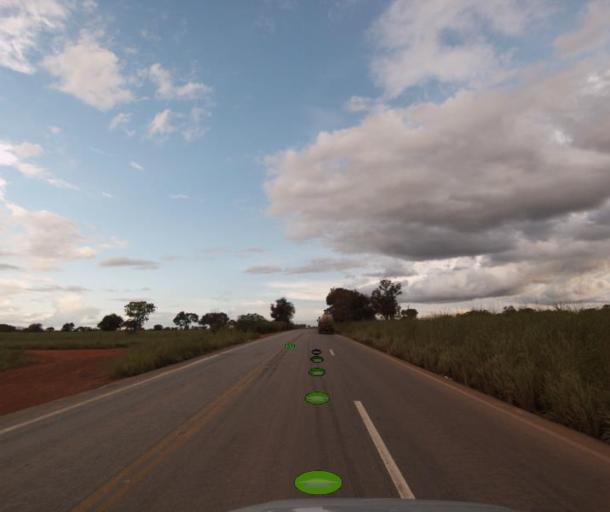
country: BR
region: Goias
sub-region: Porangatu
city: Porangatu
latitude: -13.4795
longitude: -49.1362
